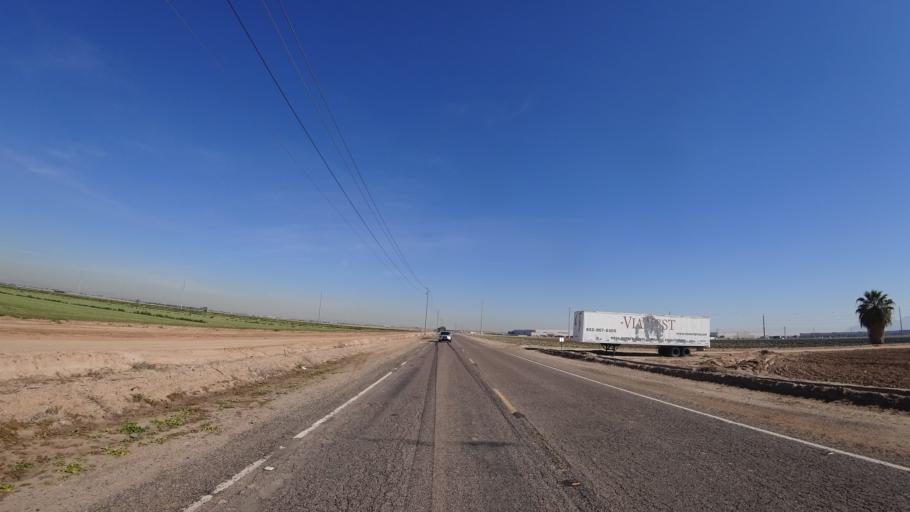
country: US
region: Arizona
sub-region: Maricopa County
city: Citrus Park
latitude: 33.5082
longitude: -112.4316
